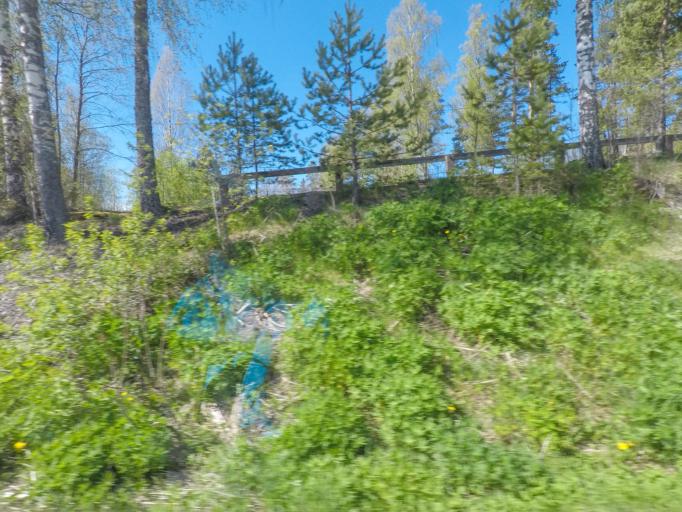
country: FI
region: Uusimaa
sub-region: Helsinki
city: Sammatti
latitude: 60.3652
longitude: 23.8073
